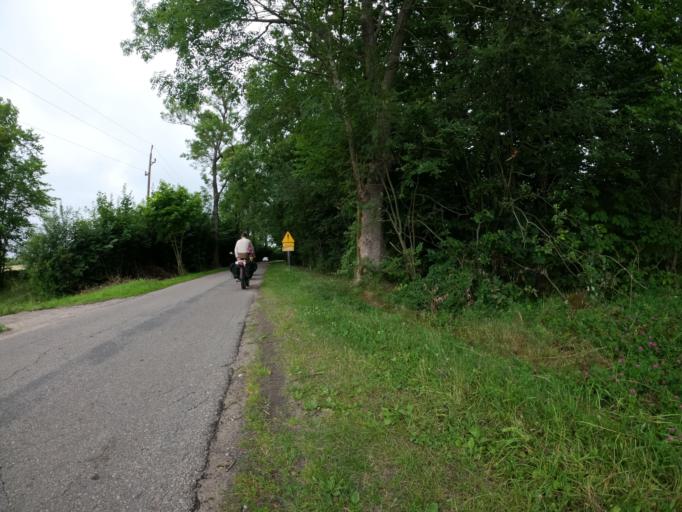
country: PL
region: West Pomeranian Voivodeship
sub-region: Powiat szczecinecki
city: Grzmiaca
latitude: 53.9362
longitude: 16.4534
